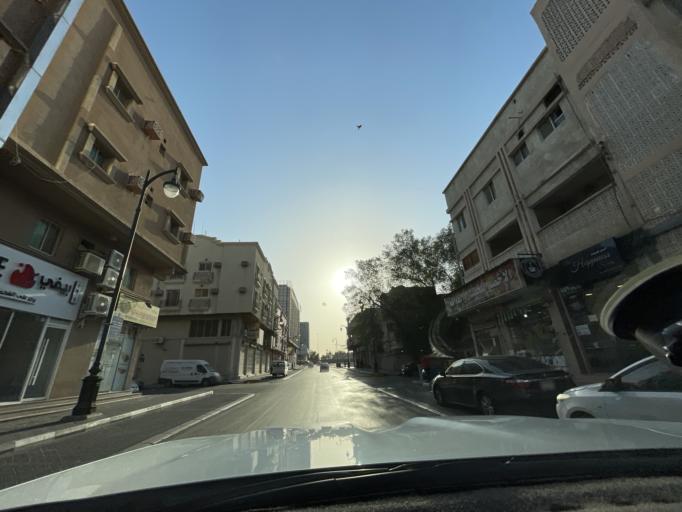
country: SA
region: Eastern Province
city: Khobar
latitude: 26.2880
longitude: 50.2083
